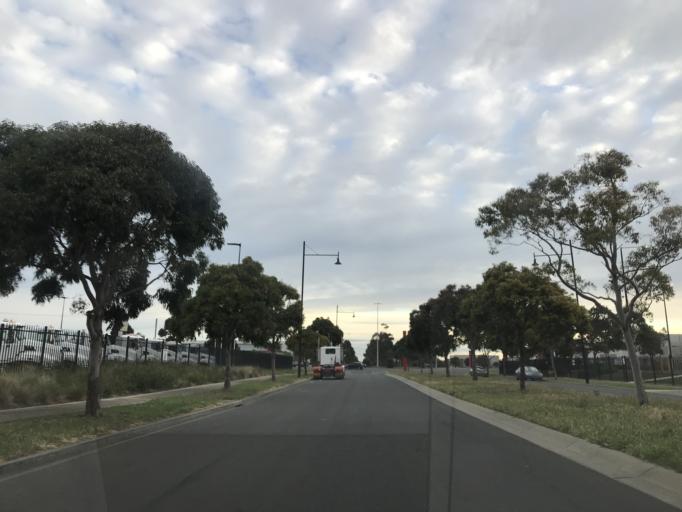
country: AU
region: Victoria
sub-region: Wyndham
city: Truganina
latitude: -37.8105
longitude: 144.7662
